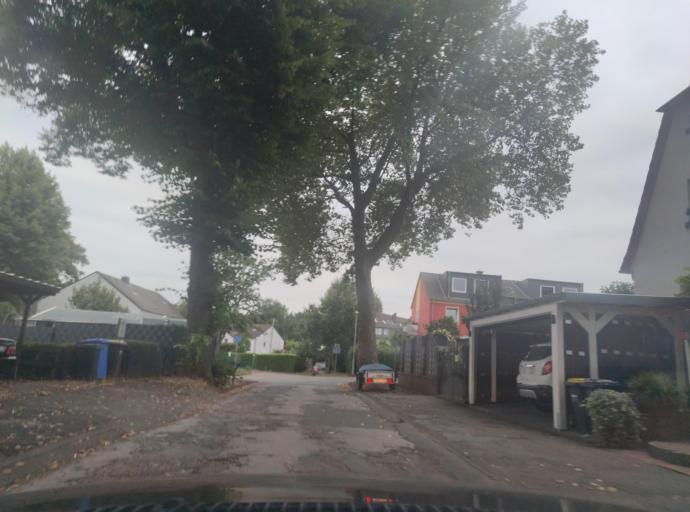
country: DE
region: North Rhine-Westphalia
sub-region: Regierungsbezirk Munster
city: Gelsenkirchen
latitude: 51.4733
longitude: 7.0785
